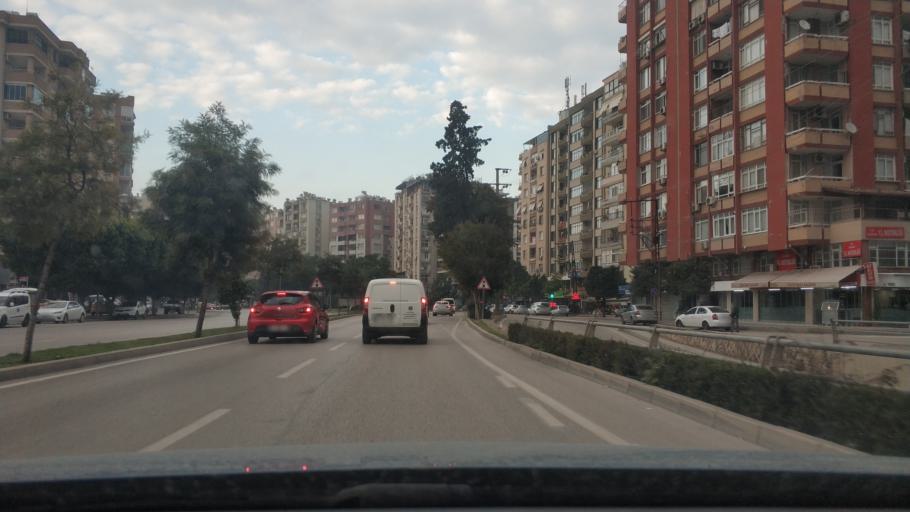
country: TR
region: Adana
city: Adana
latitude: 36.9964
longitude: 35.3182
